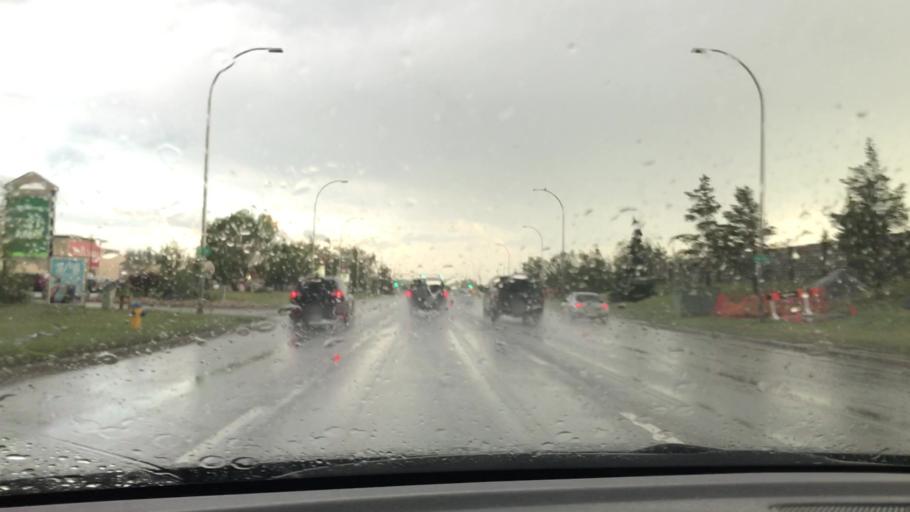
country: CA
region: Alberta
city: Edmonton
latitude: 53.4699
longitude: -113.4957
